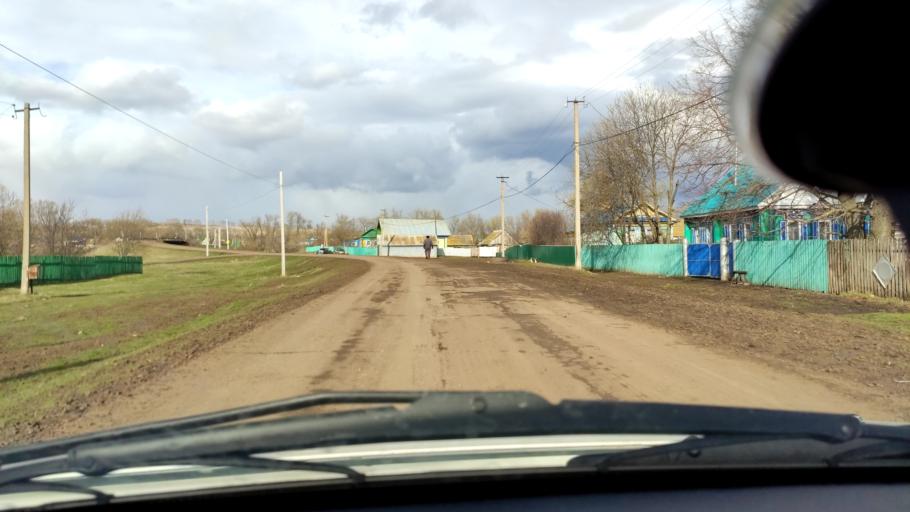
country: RU
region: Bashkortostan
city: Buzdyak
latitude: 54.7666
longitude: 54.6218
